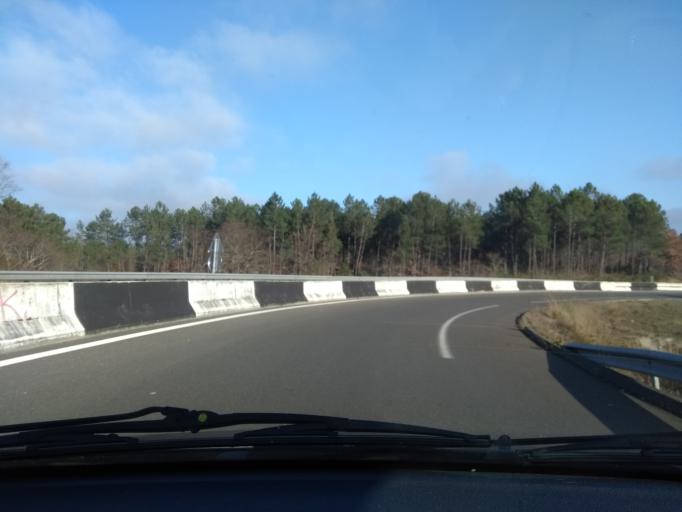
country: FR
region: Aquitaine
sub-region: Departement de la Gironde
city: Biganos
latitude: 44.6268
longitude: -0.9578
